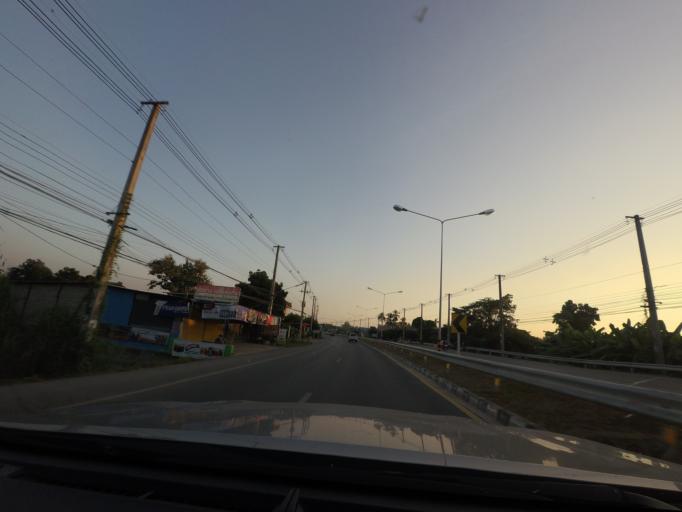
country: TH
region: Sukhothai
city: Sukhothai
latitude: 17.0437
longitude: 99.8212
